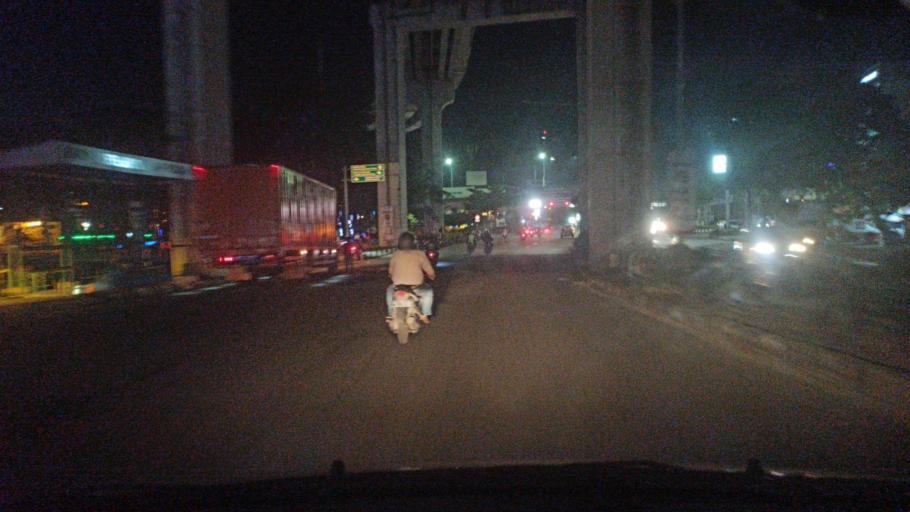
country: ID
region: South Sumatra
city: Palembang
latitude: -2.9619
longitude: 104.7371
